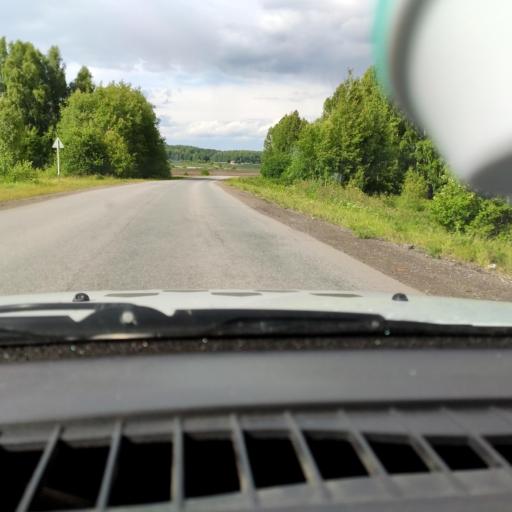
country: RU
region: Perm
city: Orda
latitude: 57.1731
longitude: 56.8261
